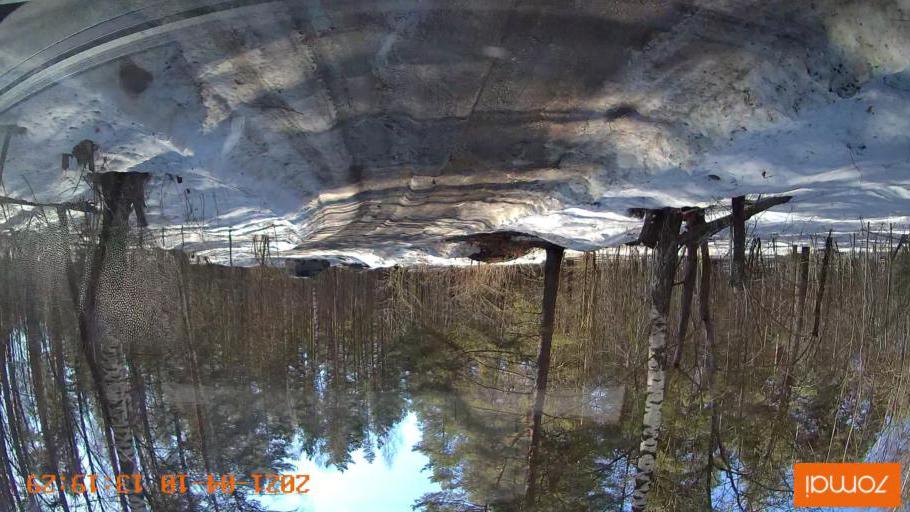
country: RU
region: Ivanovo
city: Kokhma
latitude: 56.9909
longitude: 41.0577
